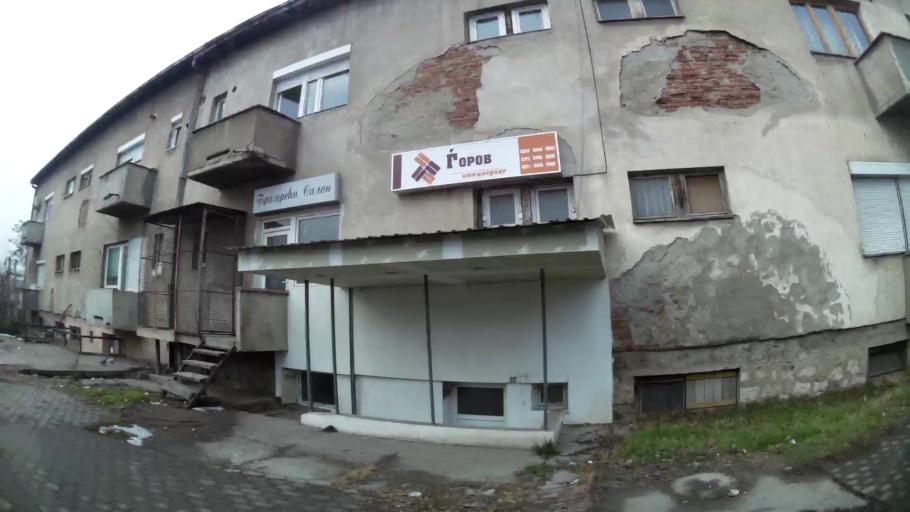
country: MK
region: Kisela Voda
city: Kisela Voda
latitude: 41.9966
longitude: 21.4940
